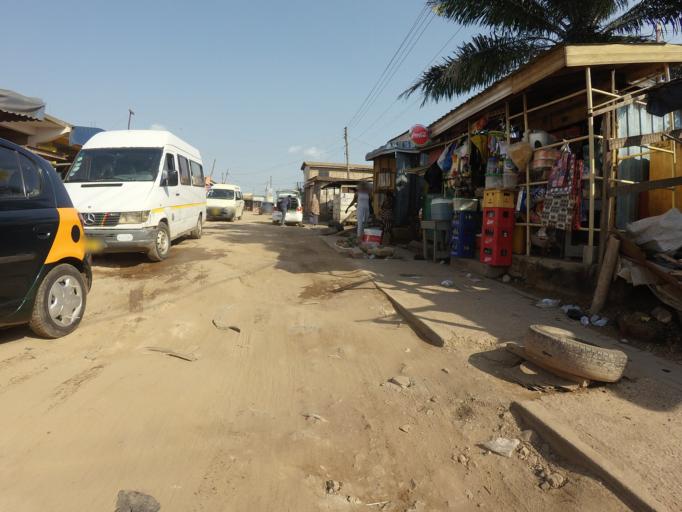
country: GH
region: Greater Accra
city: Dome
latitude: 5.6092
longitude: -0.2464
